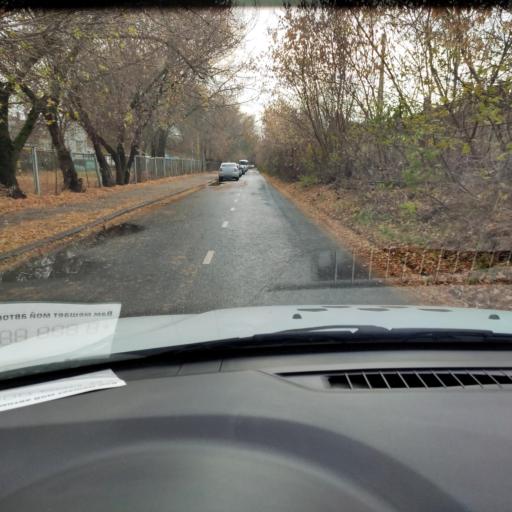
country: RU
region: Samara
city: Tol'yatti
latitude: 53.5286
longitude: 49.3908
